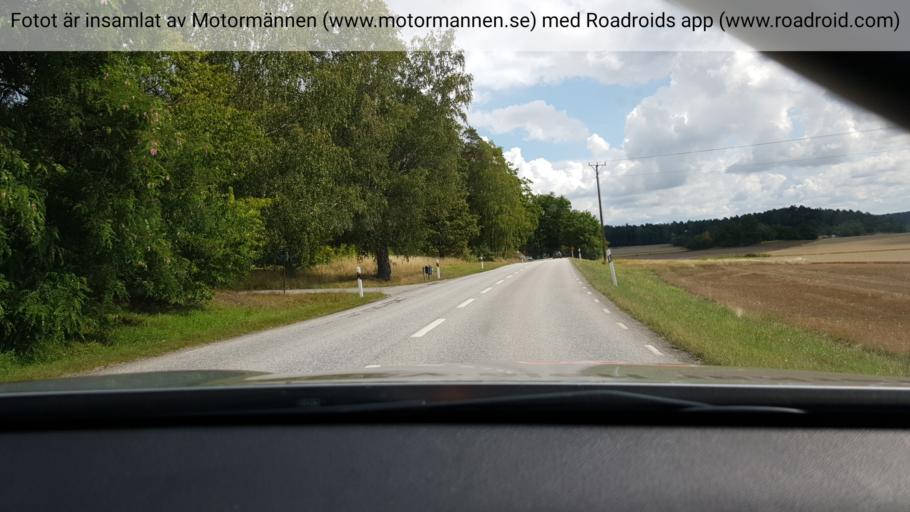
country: SE
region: Stockholm
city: Stenhamra
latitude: 59.2862
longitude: 17.7158
